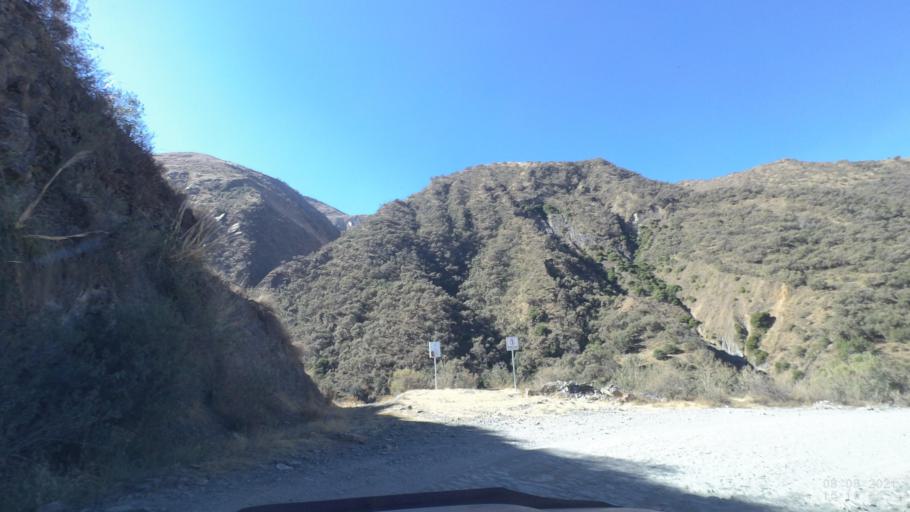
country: BO
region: Cochabamba
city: Sipe Sipe
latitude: -17.2772
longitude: -66.3206
